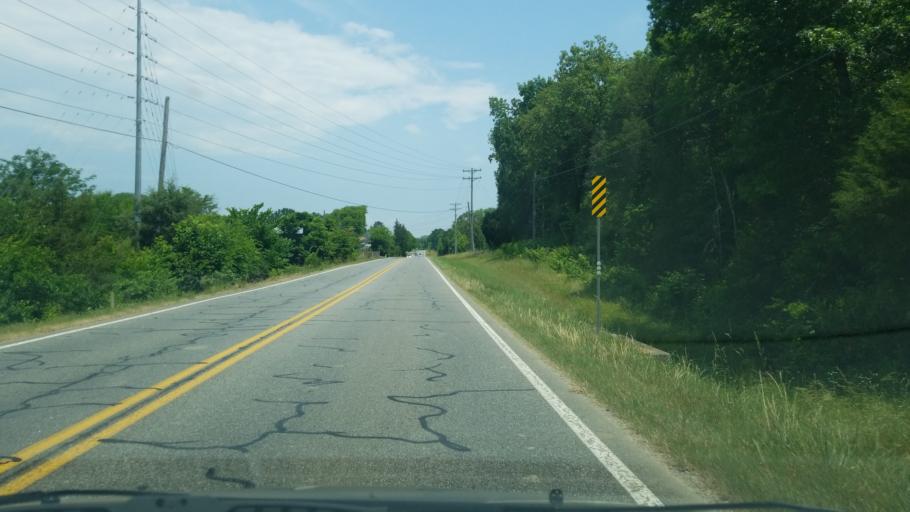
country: US
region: Tennessee
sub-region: Hamilton County
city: East Brainerd
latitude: 34.9723
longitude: -85.1002
